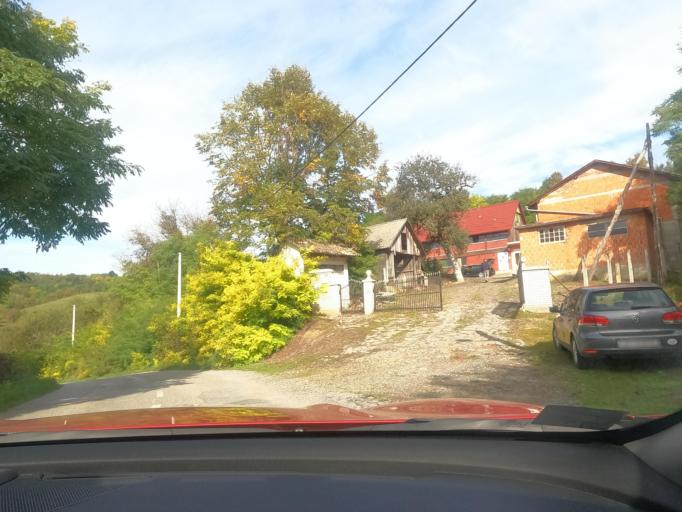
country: HR
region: Sisacko-Moslavacka
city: Glina
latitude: 45.3201
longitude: 16.2130
